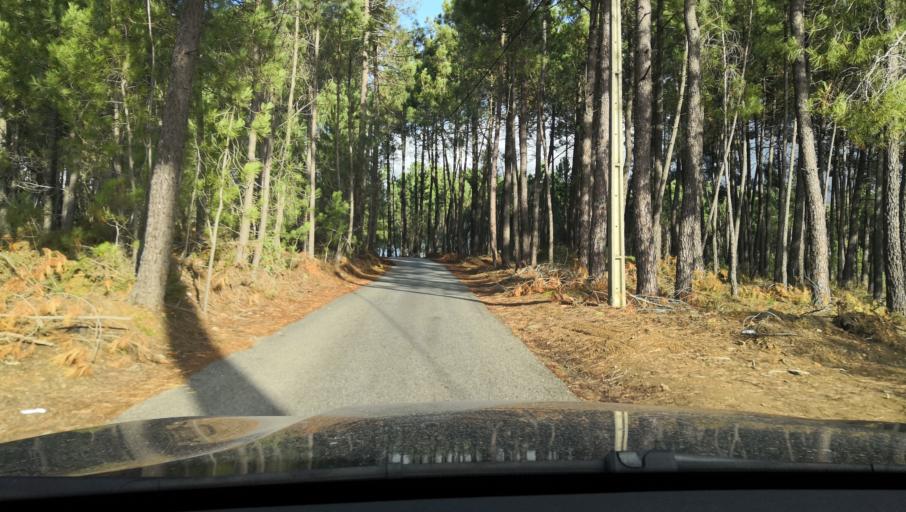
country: PT
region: Vila Real
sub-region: Vila Real
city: Vila Real
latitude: 41.2728
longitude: -7.7158
